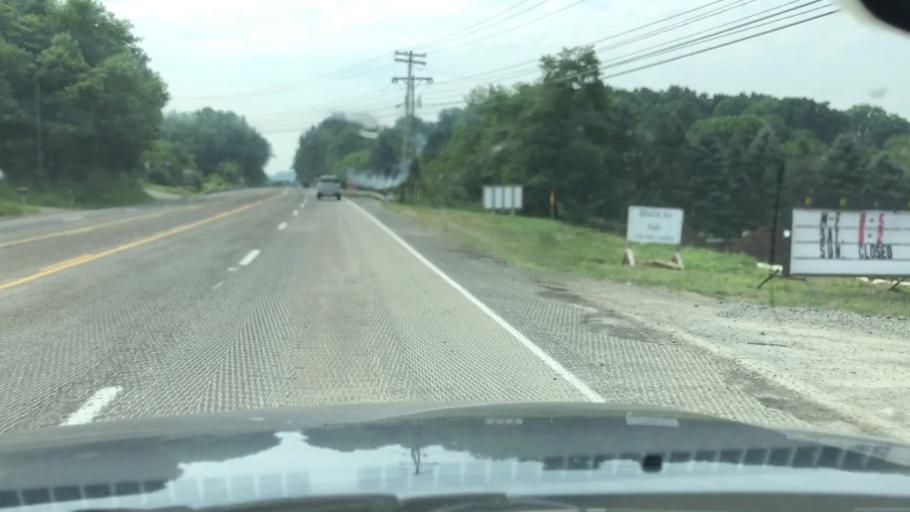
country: US
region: Pennsylvania
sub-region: Butler County
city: Nixon
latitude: 40.7420
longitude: -79.9252
